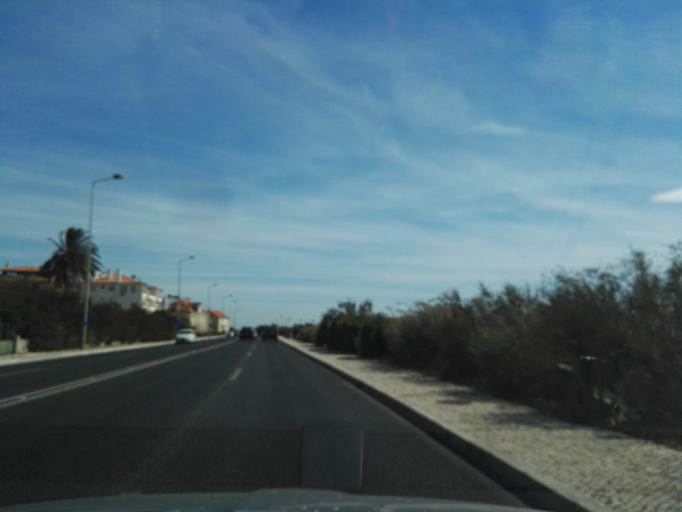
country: PT
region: Lisbon
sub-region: Cascais
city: Parede
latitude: 38.6954
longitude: -9.3766
